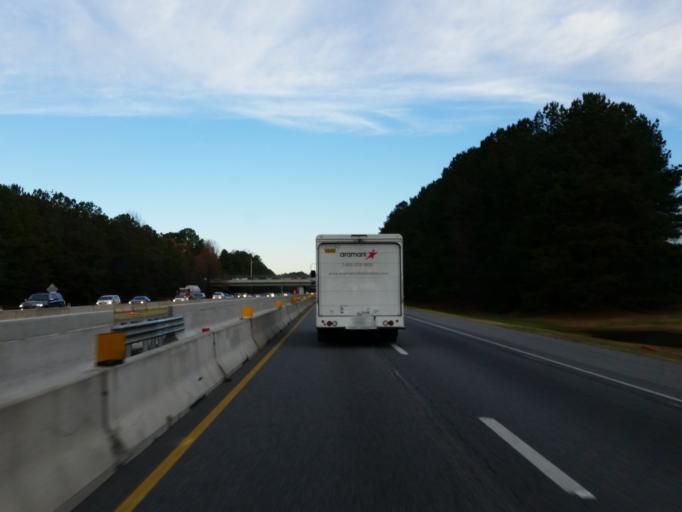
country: US
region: Georgia
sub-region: Cobb County
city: Kennesaw
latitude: 34.0346
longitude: -84.5618
